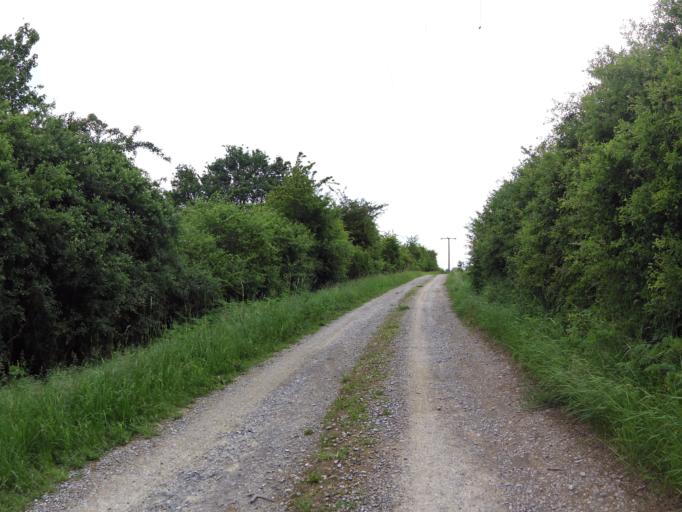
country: DE
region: Bavaria
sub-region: Regierungsbezirk Unterfranken
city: Sommerhausen
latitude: 49.7115
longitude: 10.0249
